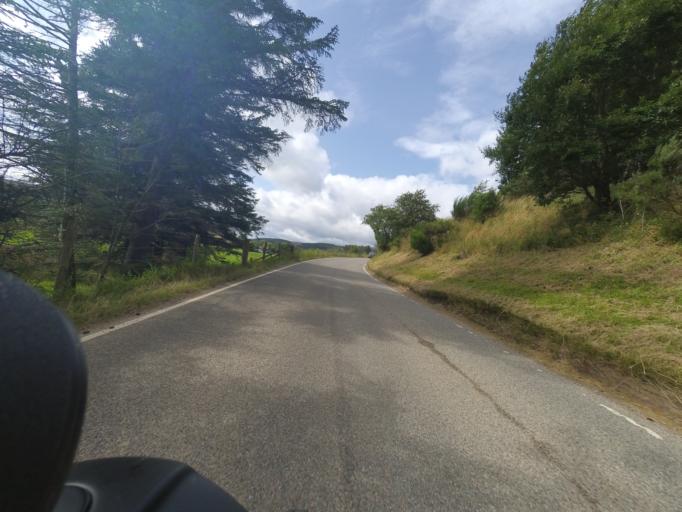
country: GB
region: Scotland
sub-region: Highland
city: Grantown on Spey
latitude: 57.2578
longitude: -3.3881
